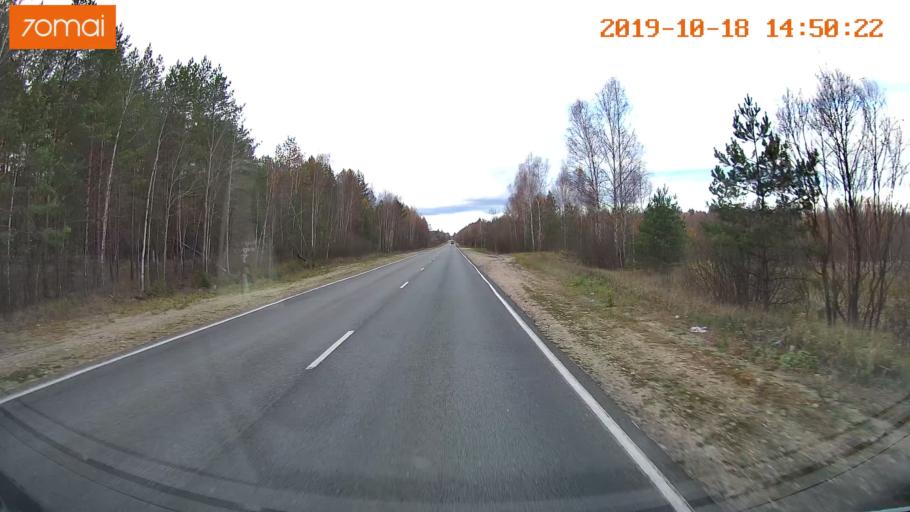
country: RU
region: Vladimir
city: Kurlovo
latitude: 55.4259
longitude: 40.6418
